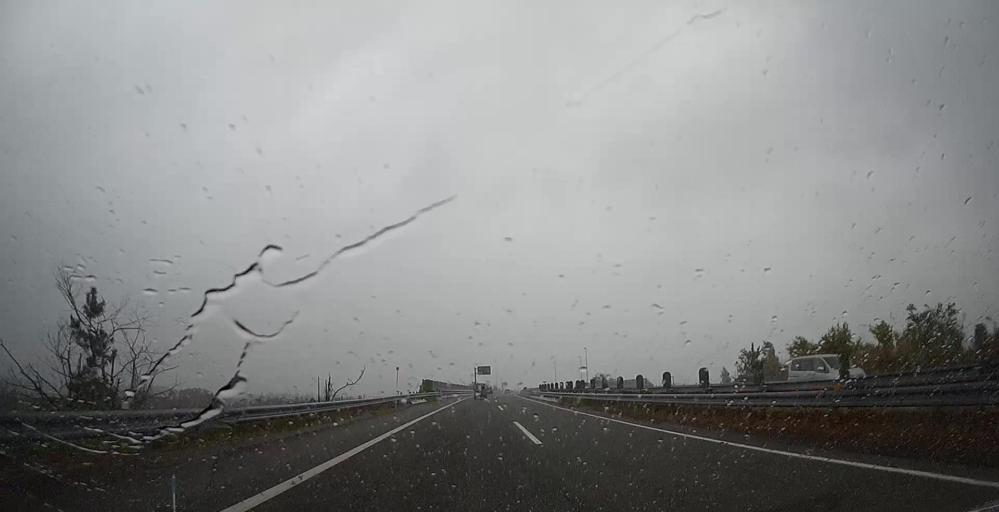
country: JP
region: Niigata
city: Shibata
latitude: 37.9599
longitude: 139.2859
